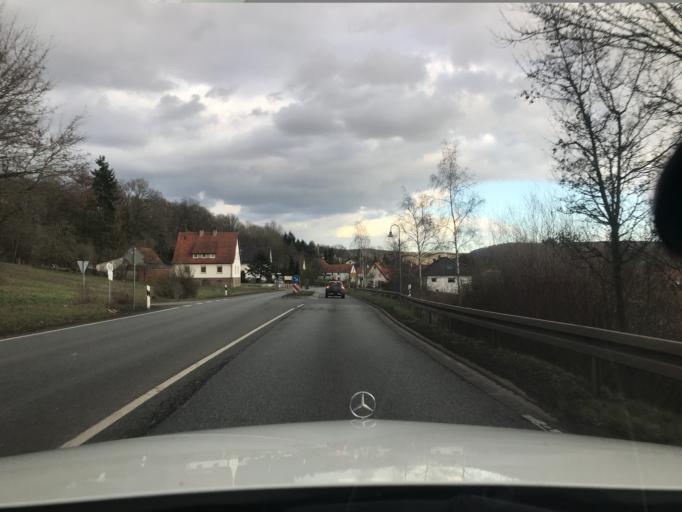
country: DE
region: Hesse
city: Waldkappel
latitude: 51.1425
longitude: 9.9303
